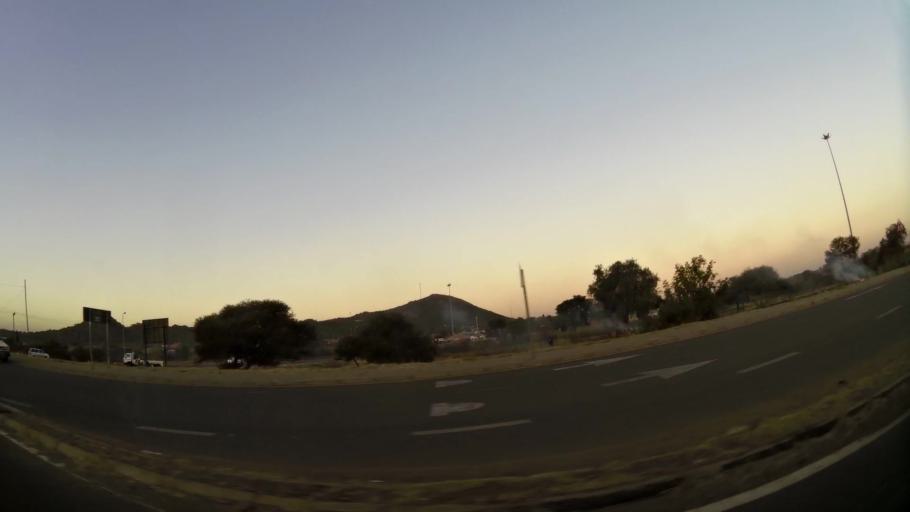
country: ZA
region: North-West
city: Ga-Rankuwa
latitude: -25.6077
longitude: 28.0048
